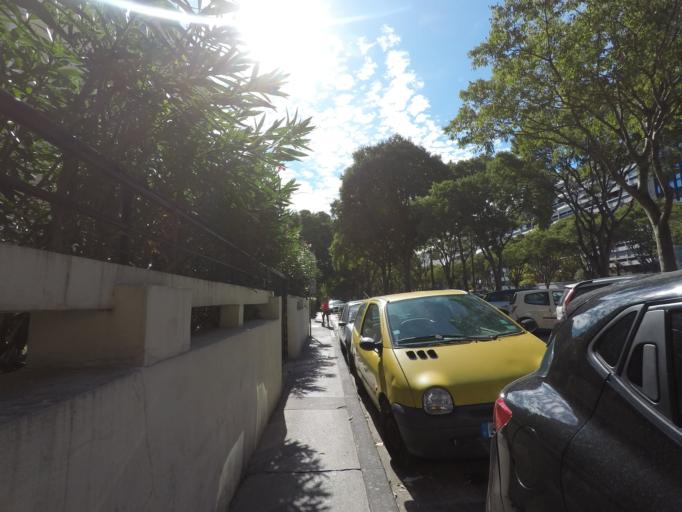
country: FR
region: Provence-Alpes-Cote d'Azur
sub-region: Departement des Bouches-du-Rhone
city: Marseille 08
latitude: 43.2712
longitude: 5.3898
